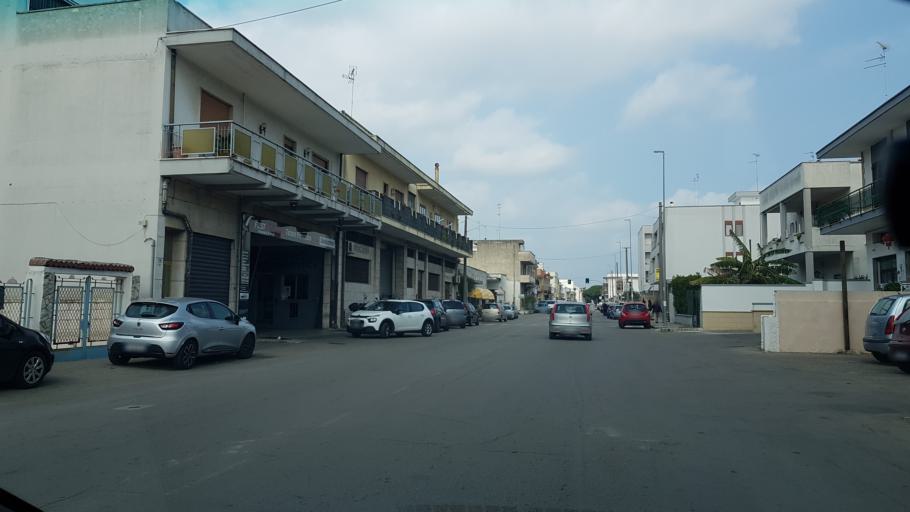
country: IT
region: Apulia
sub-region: Provincia di Lecce
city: Castromediano
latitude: 40.3329
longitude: 18.1797
